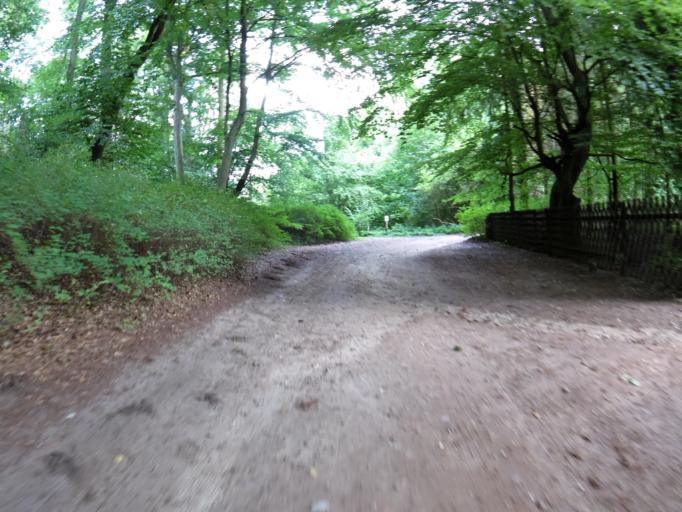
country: DE
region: Mecklenburg-Vorpommern
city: Seebad Bansin
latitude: 53.9632
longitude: 14.1080
